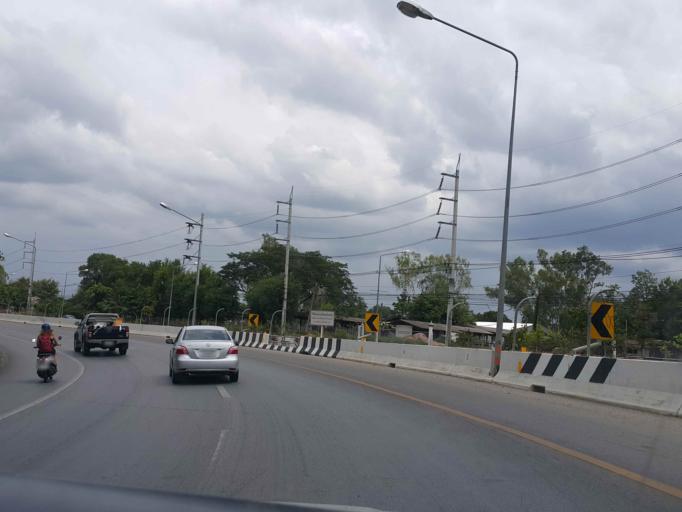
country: TH
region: Chiang Mai
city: Chiang Mai
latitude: 18.7562
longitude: 98.9411
